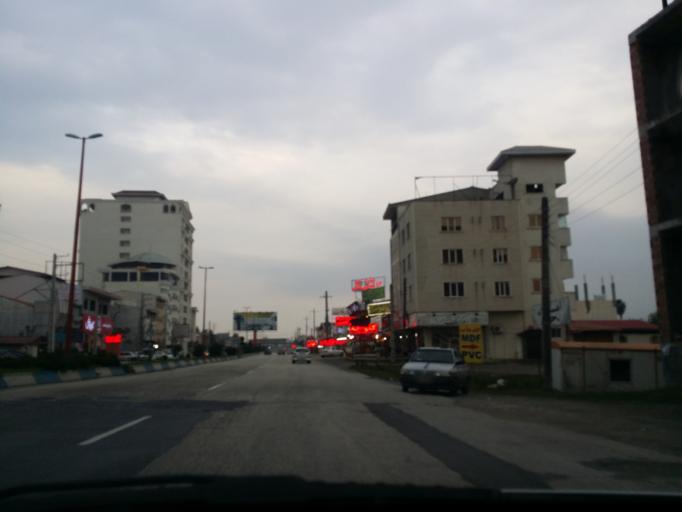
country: IR
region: Mazandaran
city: `Abbasabad
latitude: 36.7244
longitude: 51.1239
